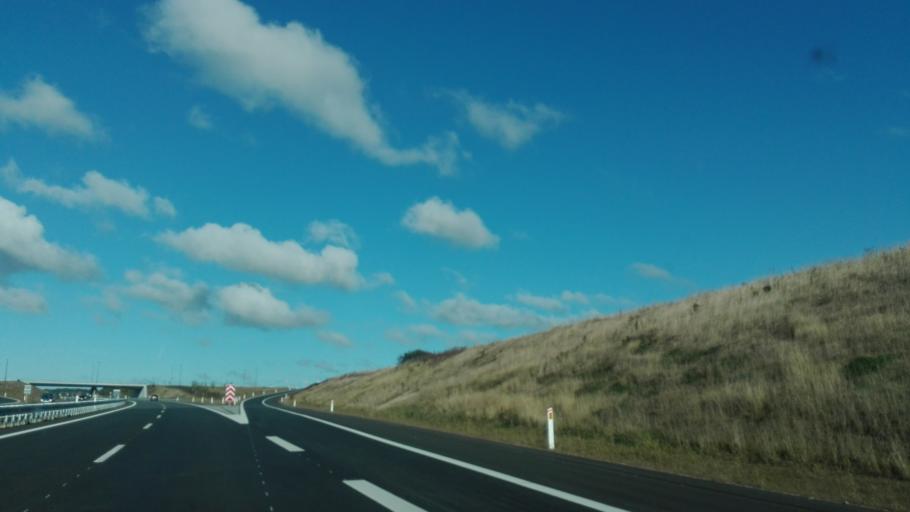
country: DK
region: Central Jutland
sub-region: Silkeborg Kommune
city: Silkeborg
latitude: 56.1987
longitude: 9.5554
